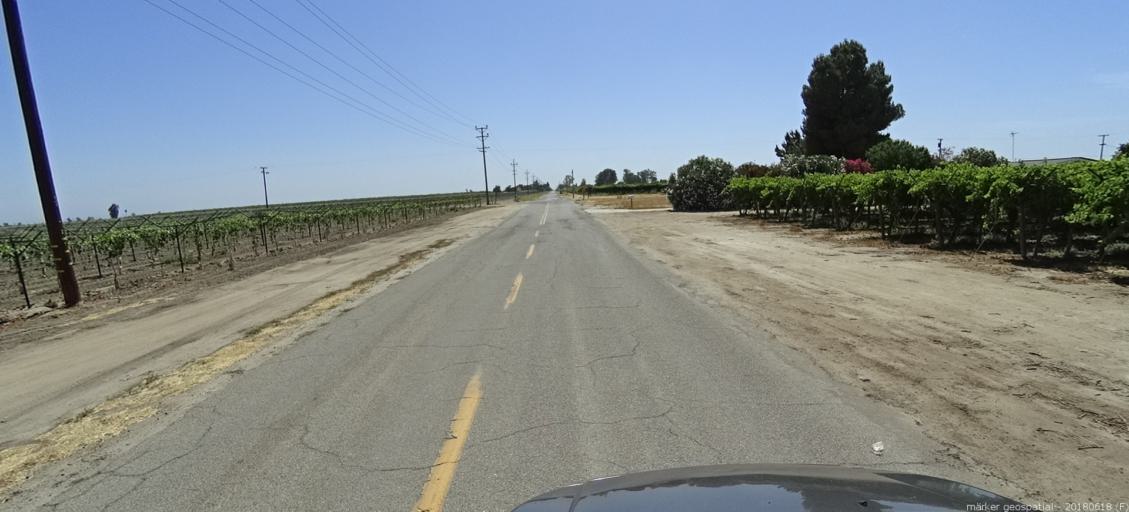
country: US
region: California
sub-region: Madera County
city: Parkwood
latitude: 36.8802
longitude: -120.1299
